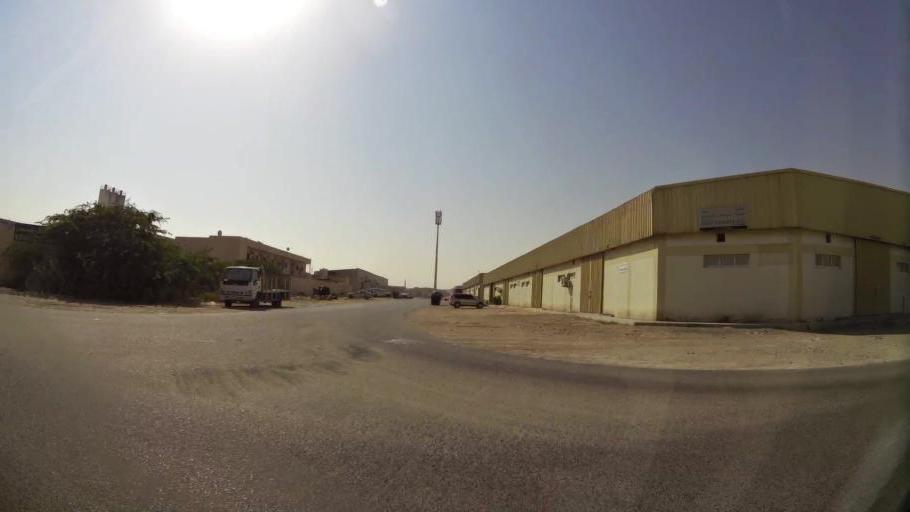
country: AE
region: Ajman
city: Ajman
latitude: 25.4381
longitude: 55.5177
